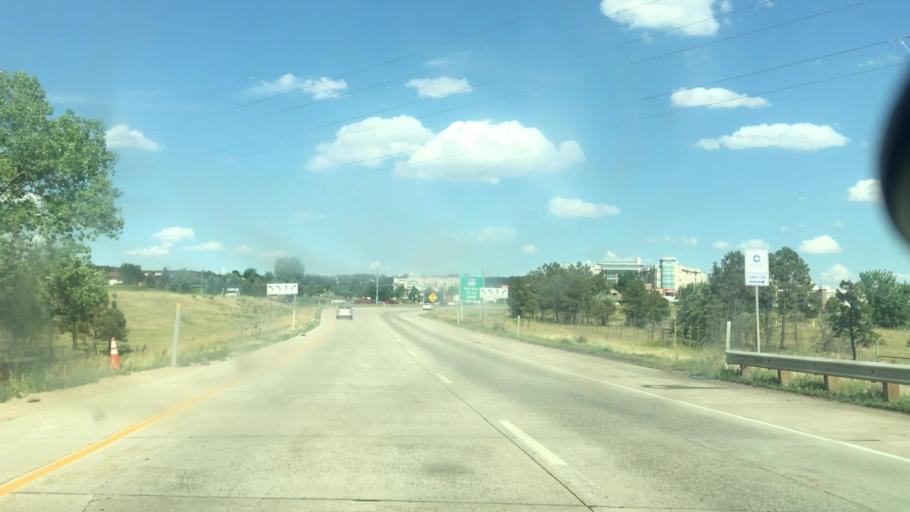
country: US
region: Colorado
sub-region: Douglas County
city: Stonegate
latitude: 39.5495
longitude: -104.7783
